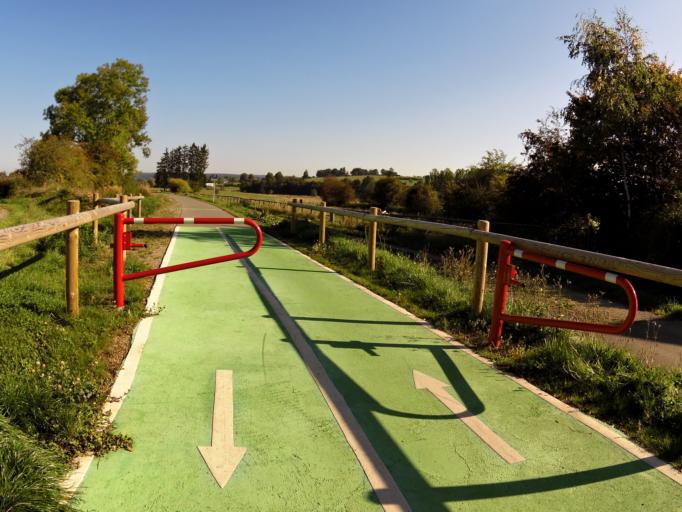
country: BE
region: Wallonia
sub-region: Province de Liege
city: Ambleve
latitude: 50.3380
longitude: 6.1198
